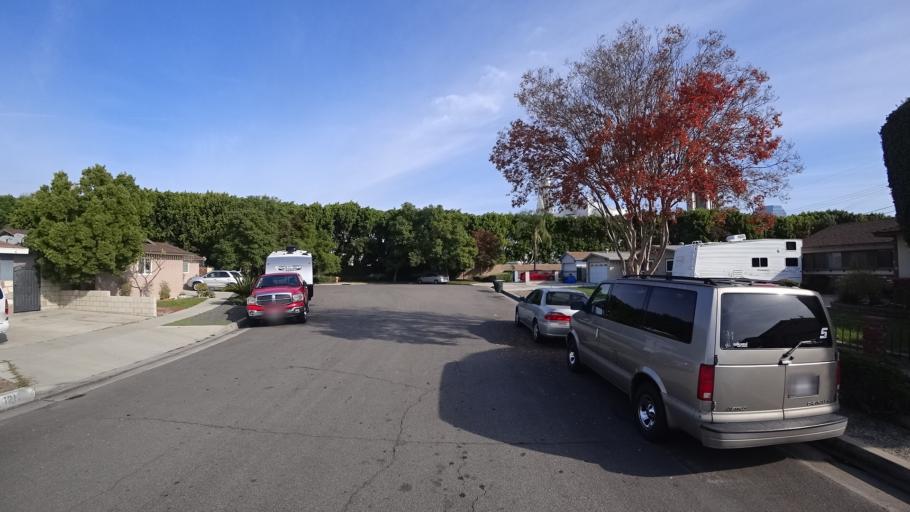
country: US
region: California
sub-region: Orange County
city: Garden Grove
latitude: 33.7863
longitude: -117.9014
